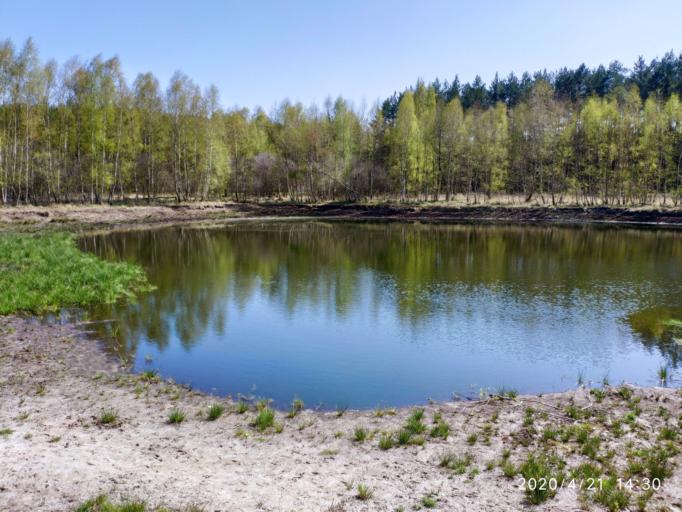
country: PL
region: Lubusz
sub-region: Powiat zielonogorski
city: Zabor
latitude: 51.9639
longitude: 15.7304
